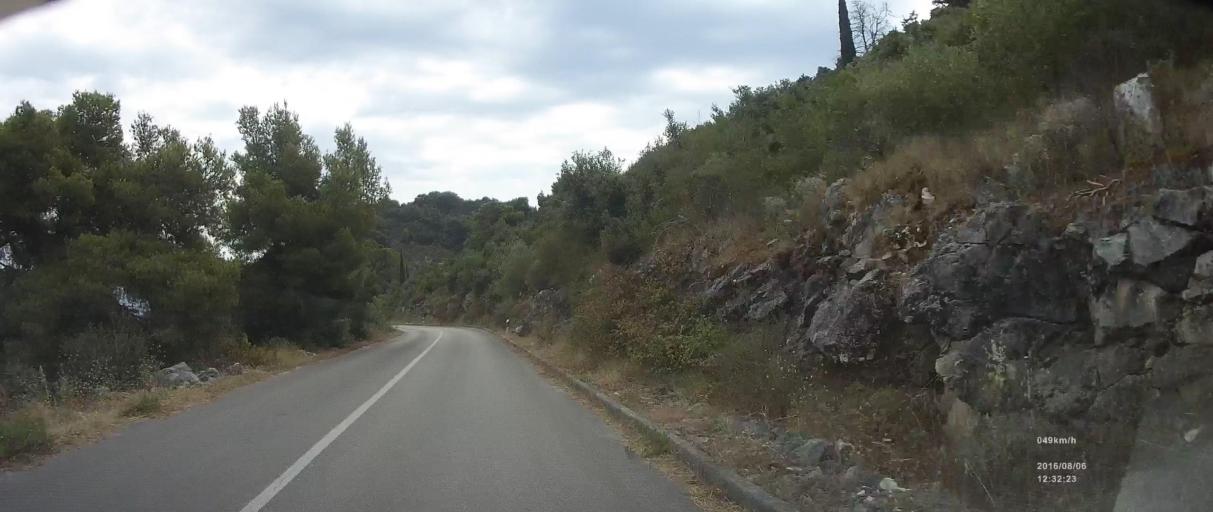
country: HR
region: Dubrovacko-Neretvanska
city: Ston
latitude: 42.7116
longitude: 17.7119
